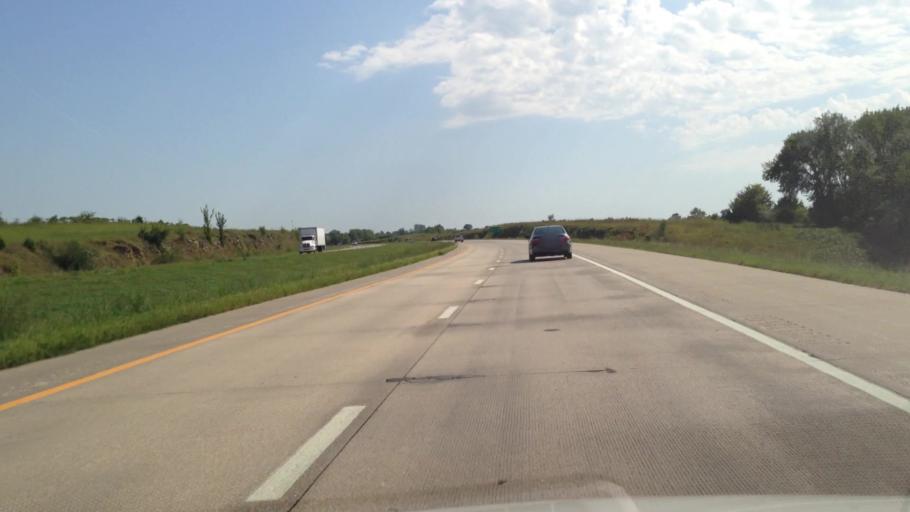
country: US
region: Kansas
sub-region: Miami County
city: Louisburg
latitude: 38.5756
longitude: -94.6965
